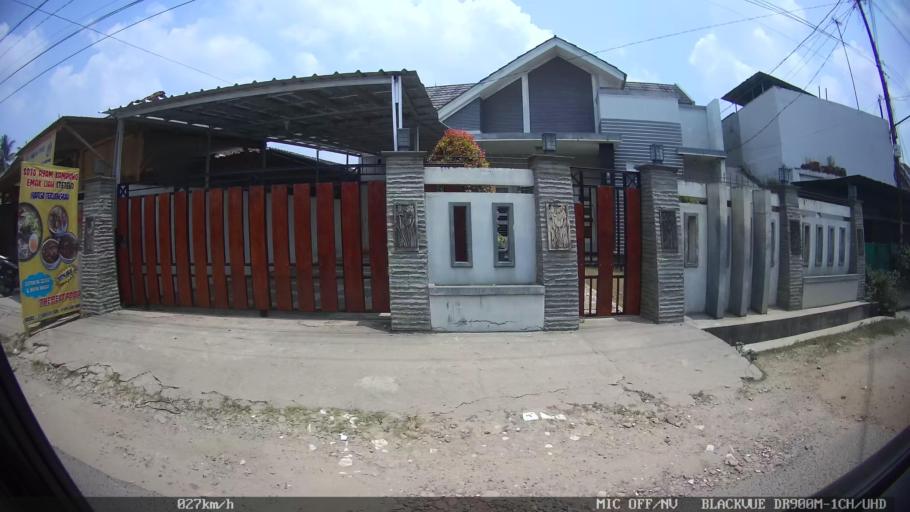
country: ID
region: Lampung
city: Pringsewu
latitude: -5.3494
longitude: 104.9815
